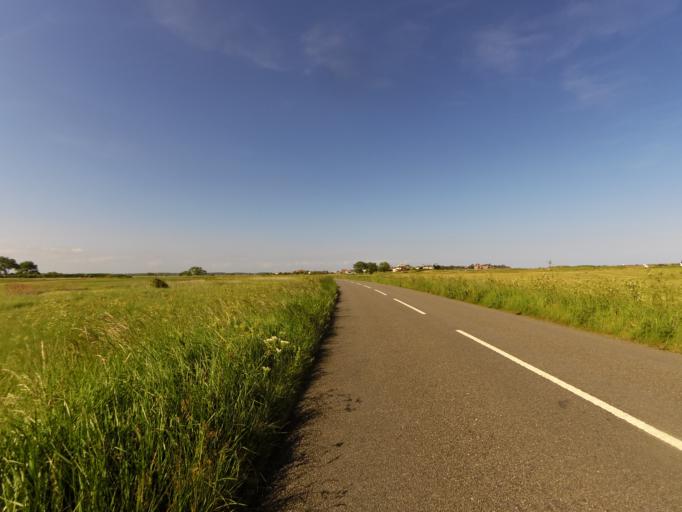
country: GB
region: England
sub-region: Suffolk
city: Felixstowe
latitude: 51.9822
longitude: 1.3857
